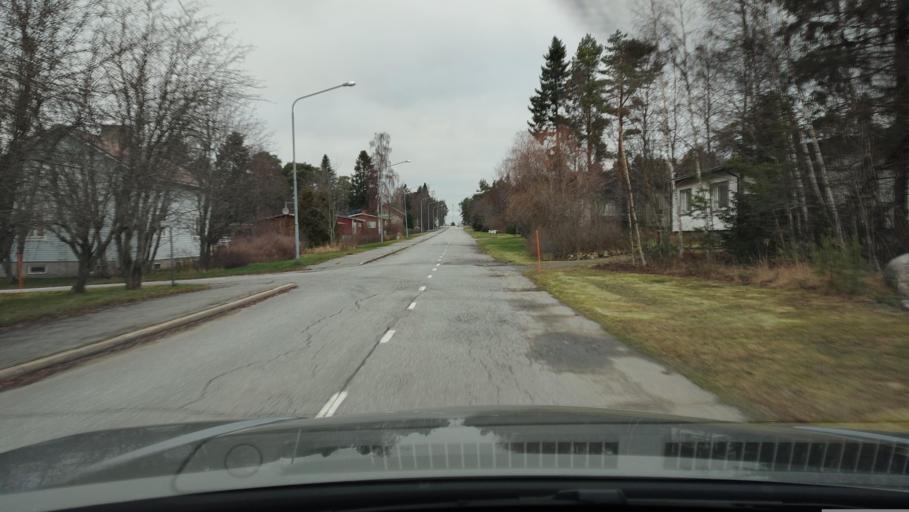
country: FI
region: Ostrobothnia
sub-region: Sydosterbotten
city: Kristinestad
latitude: 62.2679
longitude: 21.3940
